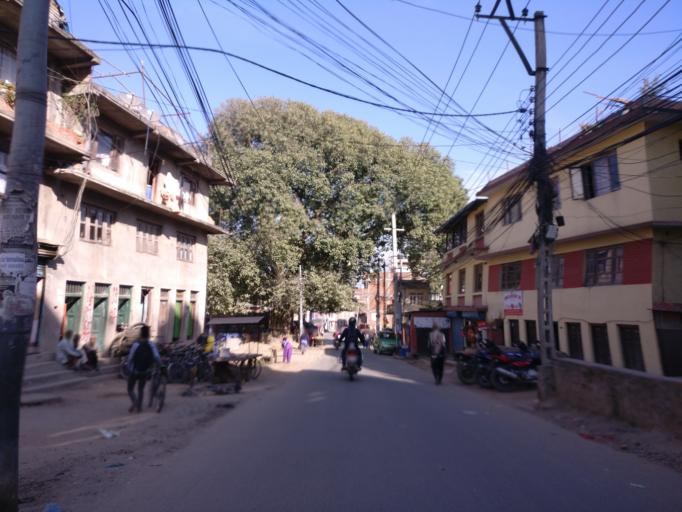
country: NP
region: Central Region
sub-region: Bagmati Zone
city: Patan
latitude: 27.6728
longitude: 85.3304
